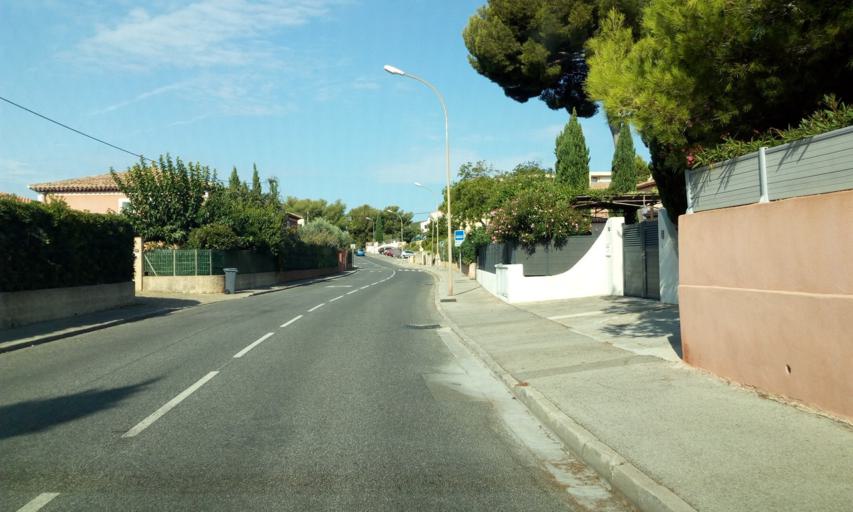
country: FR
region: Provence-Alpes-Cote d'Azur
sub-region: Departement du Var
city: Bandol
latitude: 43.1430
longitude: 5.7517
